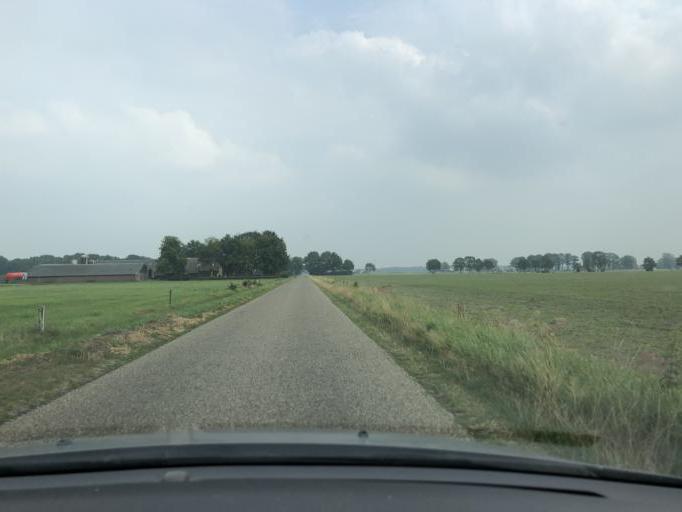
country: NL
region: Overijssel
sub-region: Gemeente Dalfsen
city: Dalfsen
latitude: 52.5982
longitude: 6.3347
